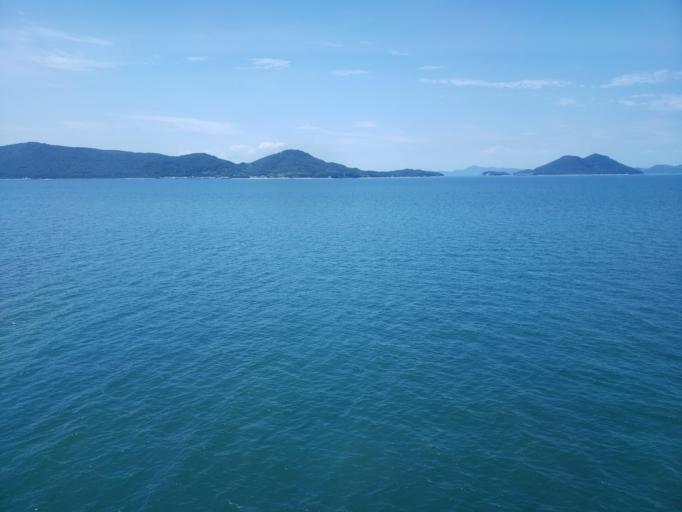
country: JP
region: Kagawa
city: Takamatsu-shi
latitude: 34.3746
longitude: 134.0795
